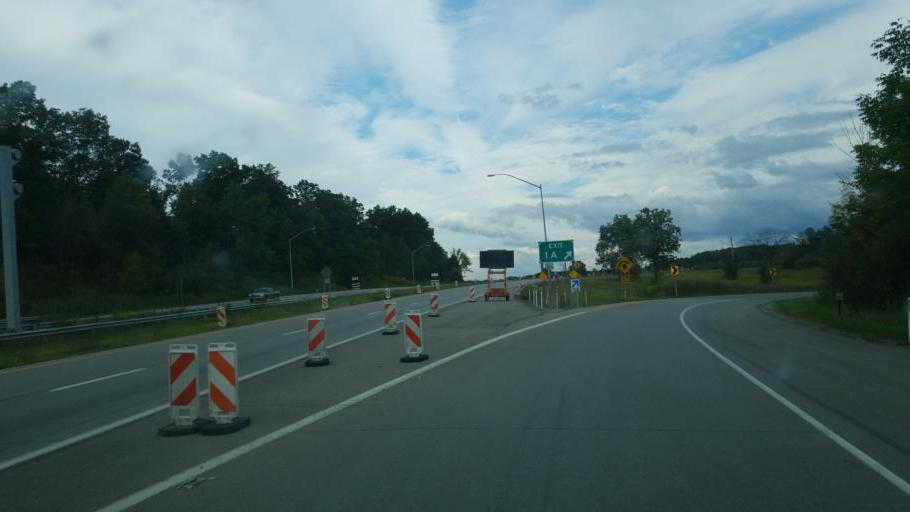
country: US
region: Pennsylvania
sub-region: Mercer County
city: Hermitage
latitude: 41.1867
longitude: -80.4494
